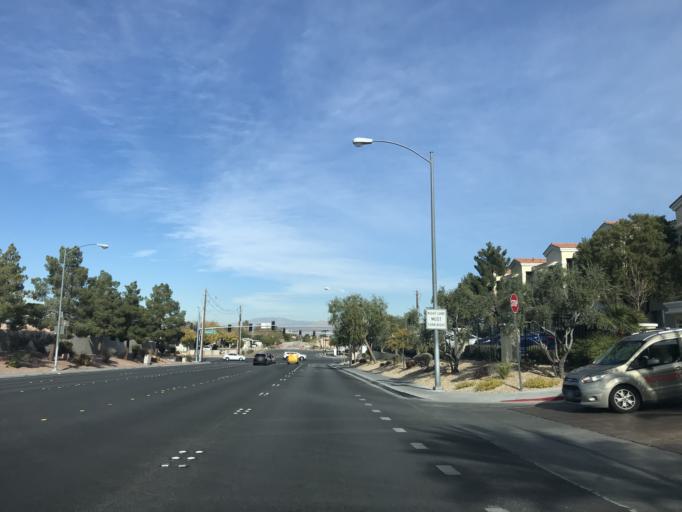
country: US
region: Nevada
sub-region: Clark County
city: Spring Valley
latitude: 36.0992
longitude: -115.2165
